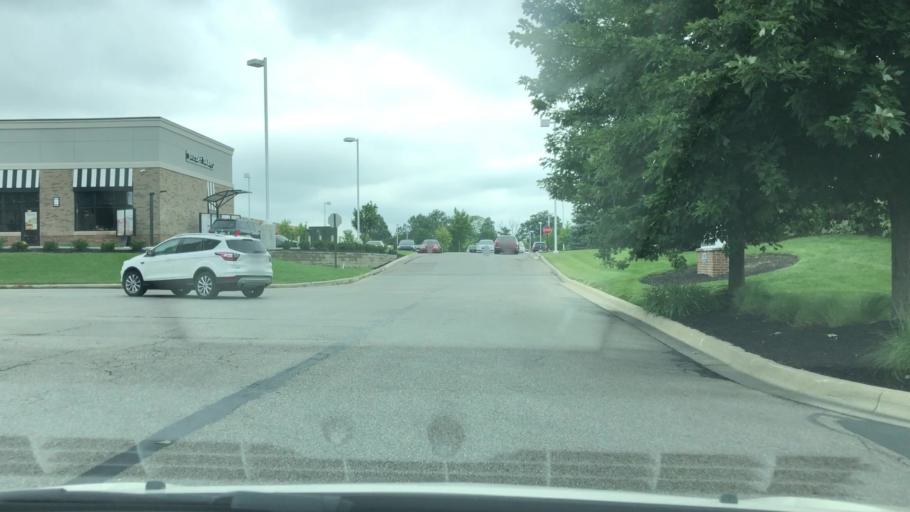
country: US
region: Ohio
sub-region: Franklin County
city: Westerville
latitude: 40.1494
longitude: -82.9776
